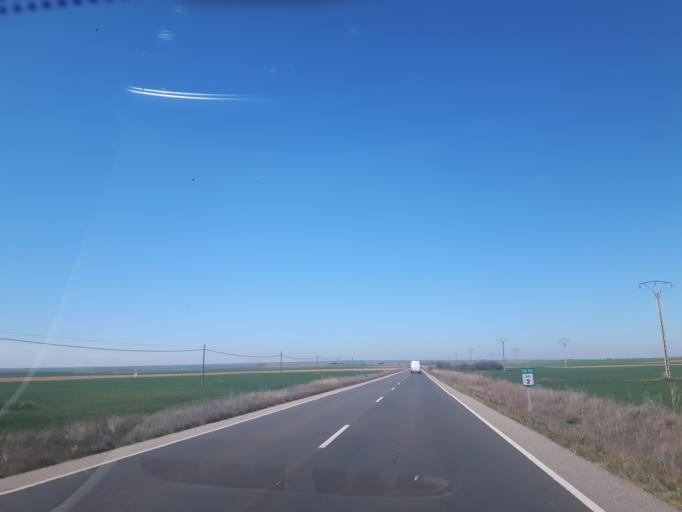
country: ES
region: Castille and Leon
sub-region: Provincia de Salamanca
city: Penaranda de Bracamonte
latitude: 40.8959
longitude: -5.2362
